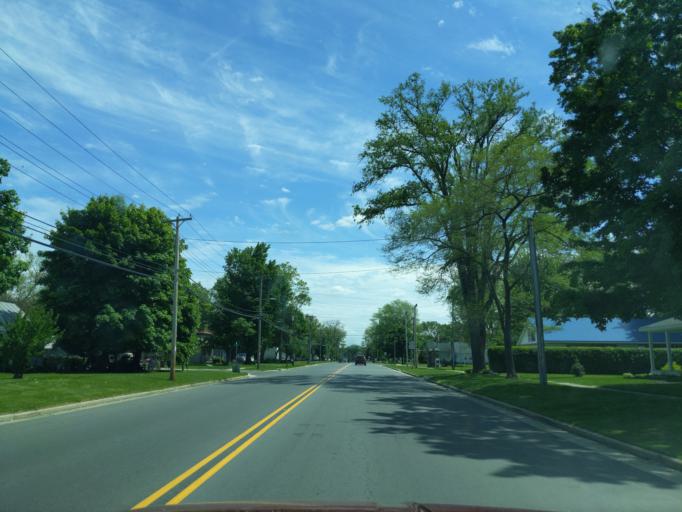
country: US
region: Wisconsin
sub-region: Columbia County
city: Pardeeville
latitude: 43.5431
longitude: -89.3022
